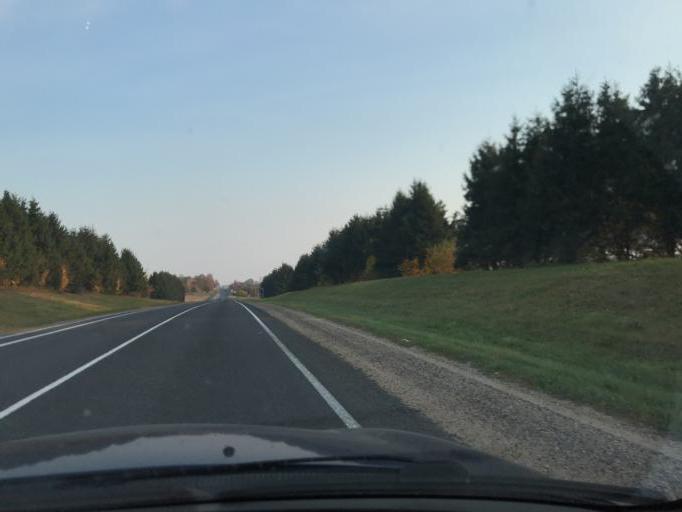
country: BY
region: Grodnenskaya
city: Karelichy
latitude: 53.5806
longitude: 26.1216
